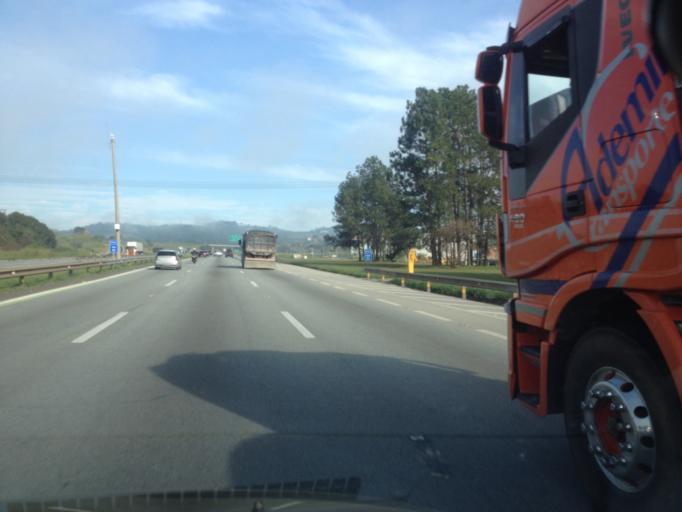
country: BR
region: Sao Paulo
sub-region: Sao Roque
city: Sao Roque
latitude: -23.4372
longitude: -47.0989
